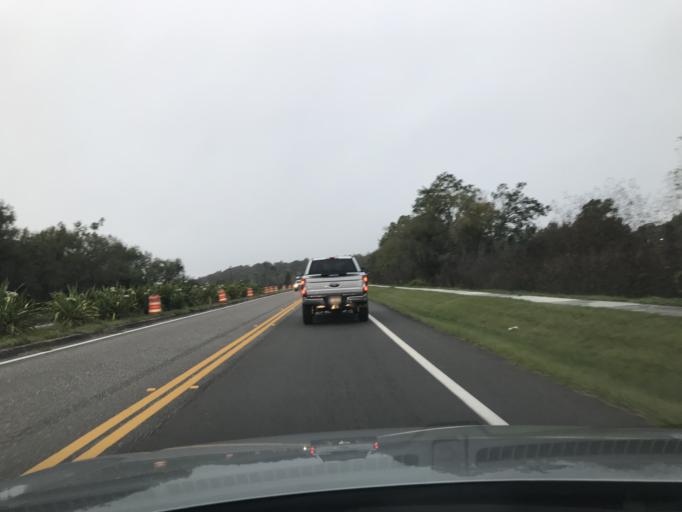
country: US
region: Florida
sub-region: Pinellas County
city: Oldsmar
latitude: 28.0535
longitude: -82.6554
